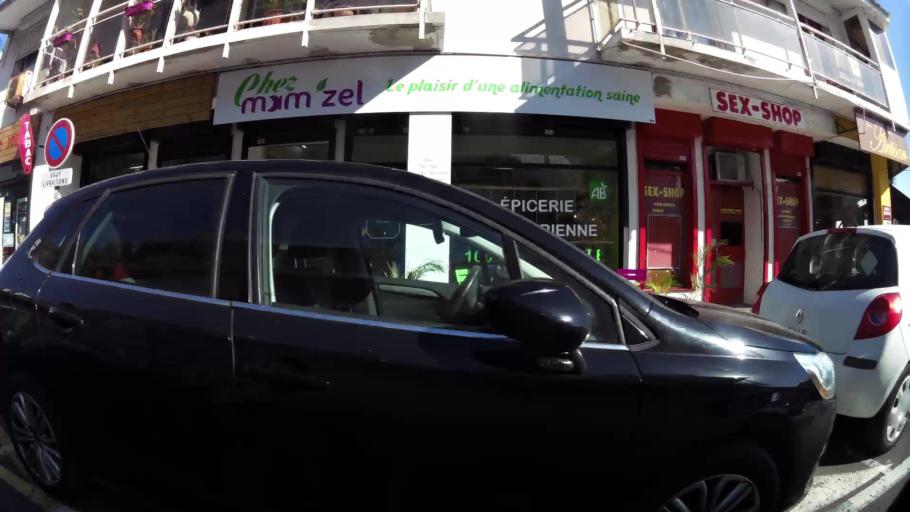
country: RE
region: Reunion
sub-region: Reunion
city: Saint-Pierre
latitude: -21.3408
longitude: 55.4692
